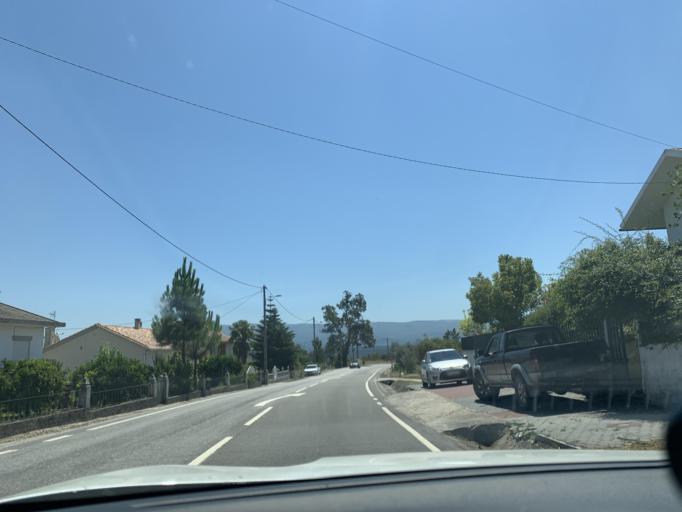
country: PT
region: Viseu
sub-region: Mangualde
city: Mangualde
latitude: 40.5702
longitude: -7.7242
